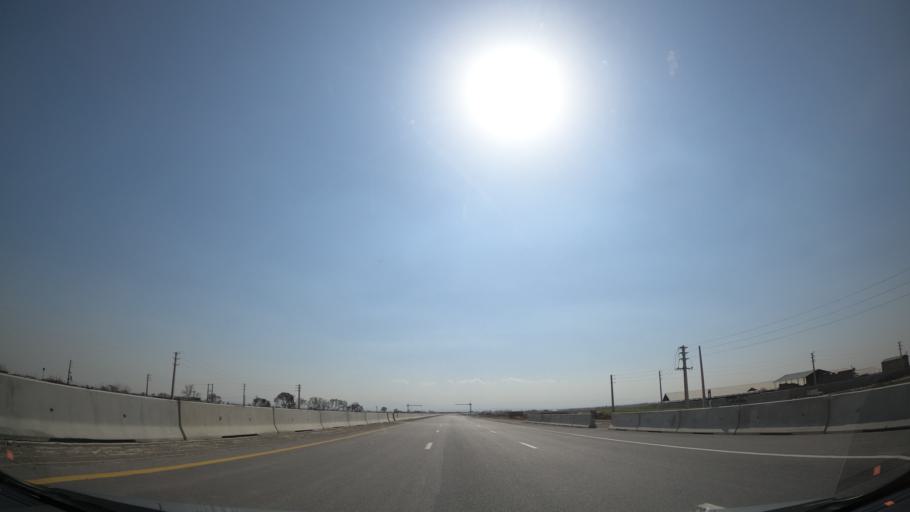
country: IR
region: Qazvin
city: Abyek
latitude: 35.9925
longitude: 50.4620
